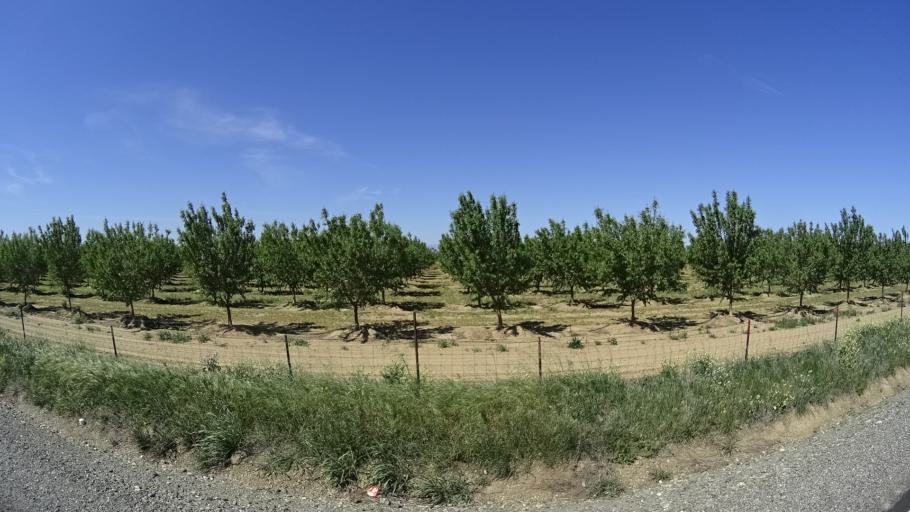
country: US
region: California
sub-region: Glenn County
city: Orland
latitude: 39.6617
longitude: -122.1407
